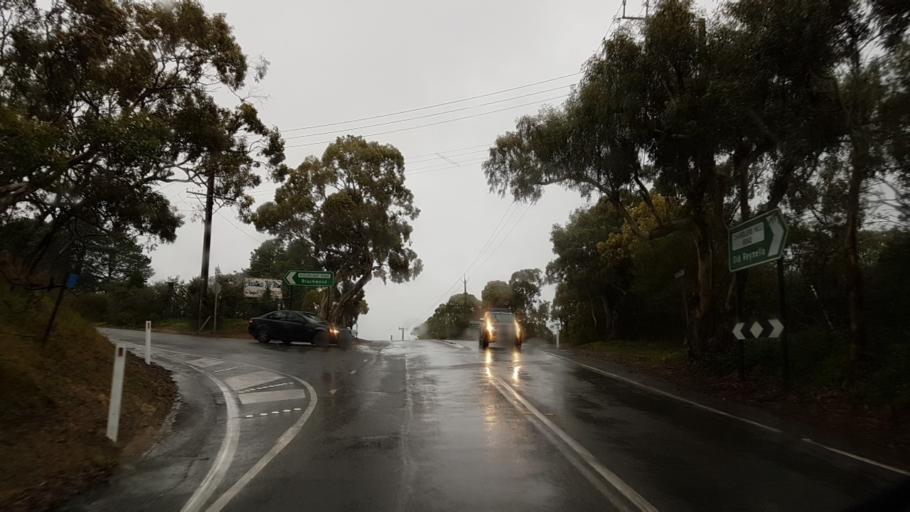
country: AU
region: South Australia
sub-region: Onkaparinga
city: Craigburn Farm
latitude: -35.0875
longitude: 138.6127
